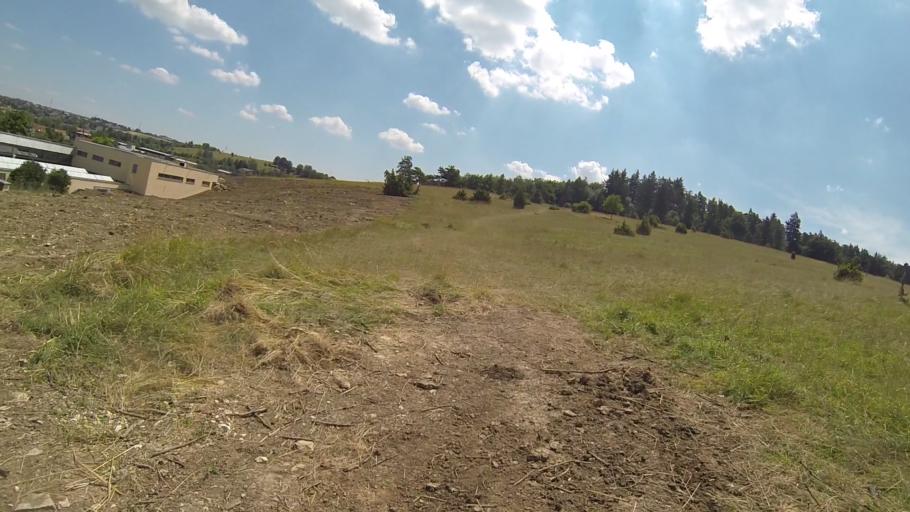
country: DE
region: Baden-Wuerttemberg
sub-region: Regierungsbezirk Stuttgart
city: Herbrechtingen
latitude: 48.6170
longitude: 10.1712
